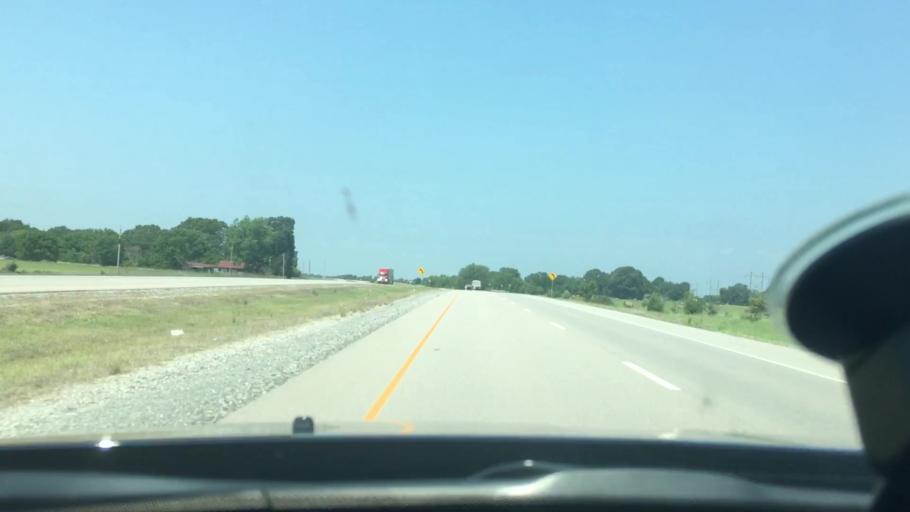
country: US
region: Oklahoma
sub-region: Atoka County
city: Atoka
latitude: 34.3331
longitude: -96.0529
